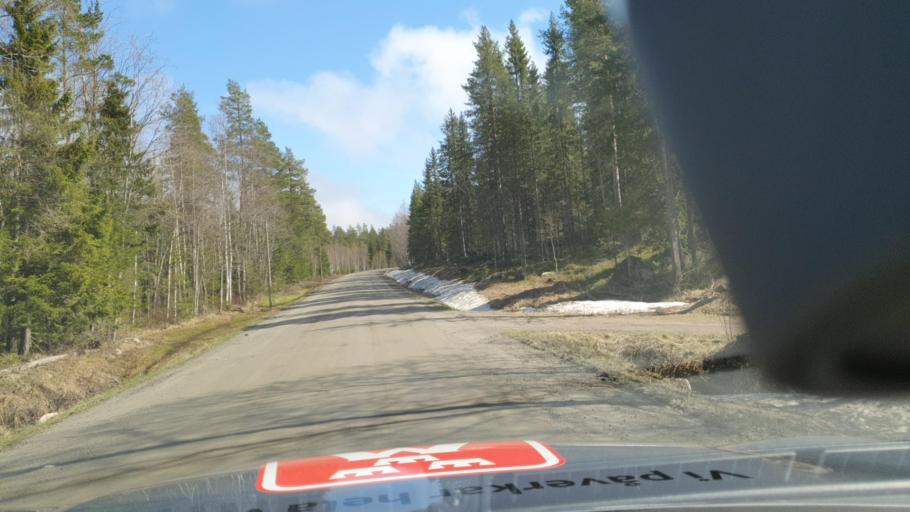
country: SE
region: Vaesterbotten
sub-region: Bjurholms Kommun
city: Bjurholm
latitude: 63.6852
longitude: 18.9674
